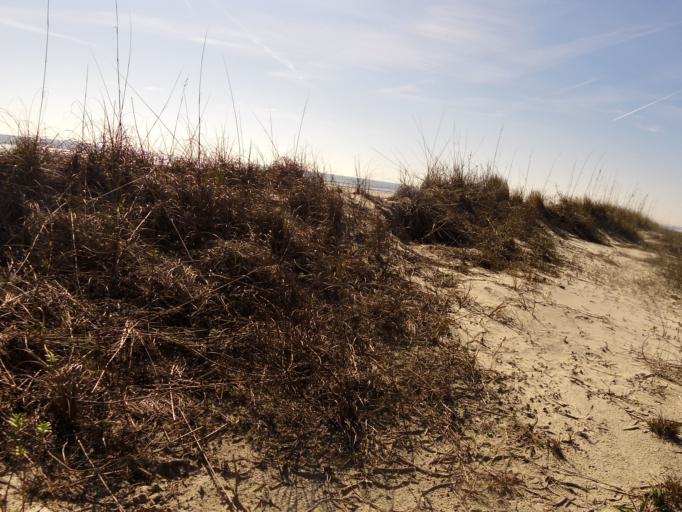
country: US
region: South Carolina
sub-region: Charleston County
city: Isle of Palms
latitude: 32.7985
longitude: -79.7498
